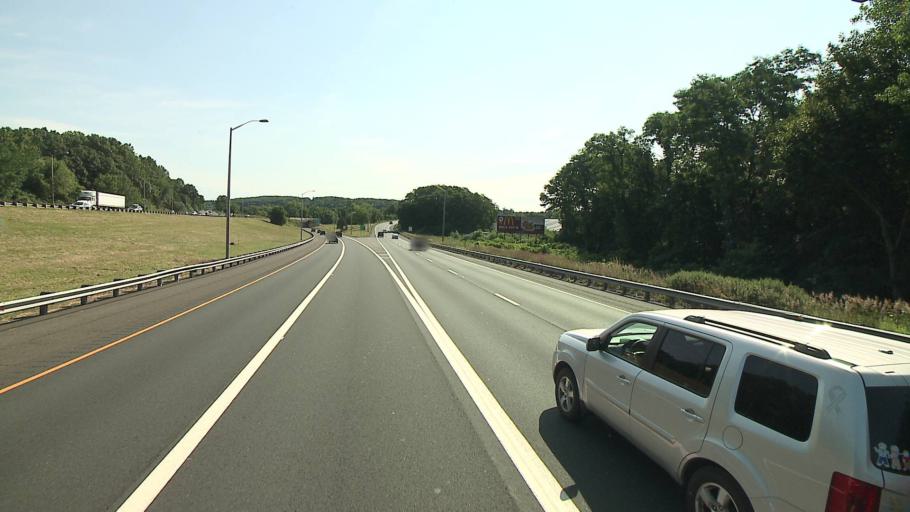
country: US
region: Connecticut
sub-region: Fairfield County
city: Danbury
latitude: 41.4171
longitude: -73.4284
